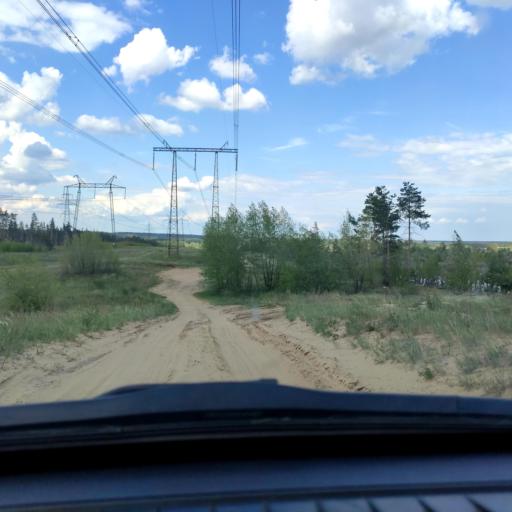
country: RU
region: Samara
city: Zhigulevsk
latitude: 53.5366
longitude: 49.5479
